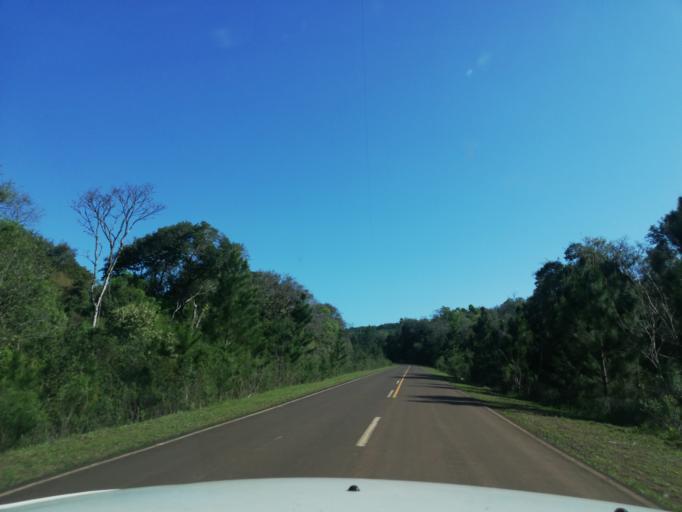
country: AR
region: Misiones
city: Arroyo del Medio
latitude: -27.6678
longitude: -55.3998
